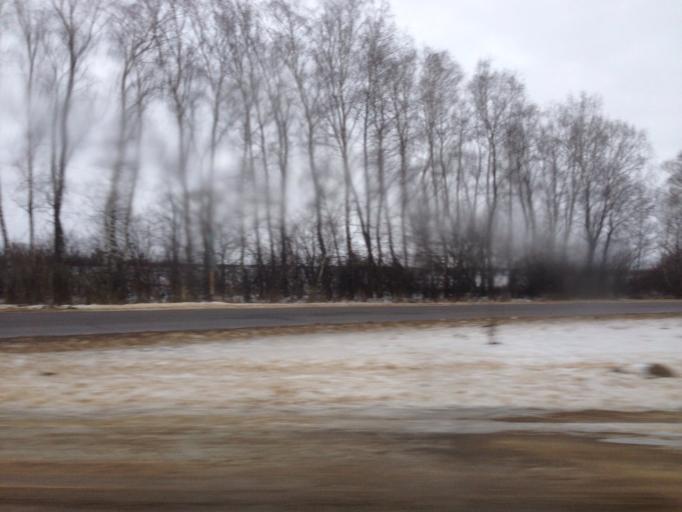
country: RU
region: Tula
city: Kamenetskiy
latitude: 53.9928
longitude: 38.2126
